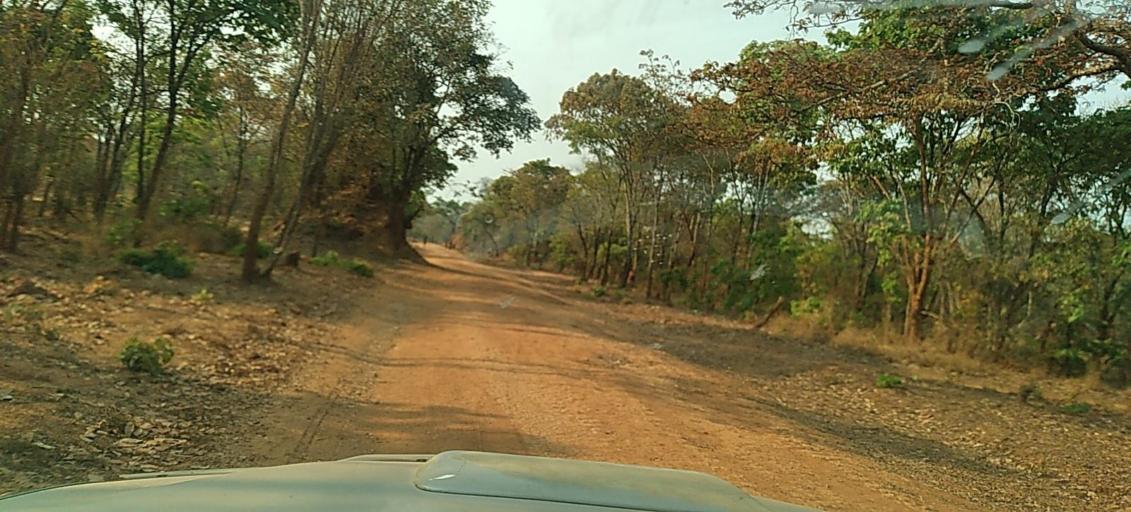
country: ZM
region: North-Western
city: Kasempa
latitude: -13.2875
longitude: 26.5551
